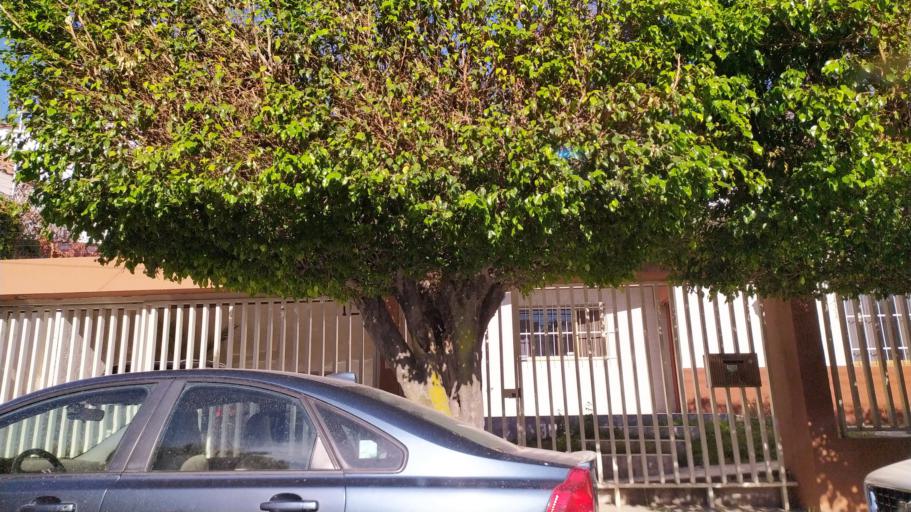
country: MX
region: Jalisco
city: Guadalajara
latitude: 20.6660
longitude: -103.4271
